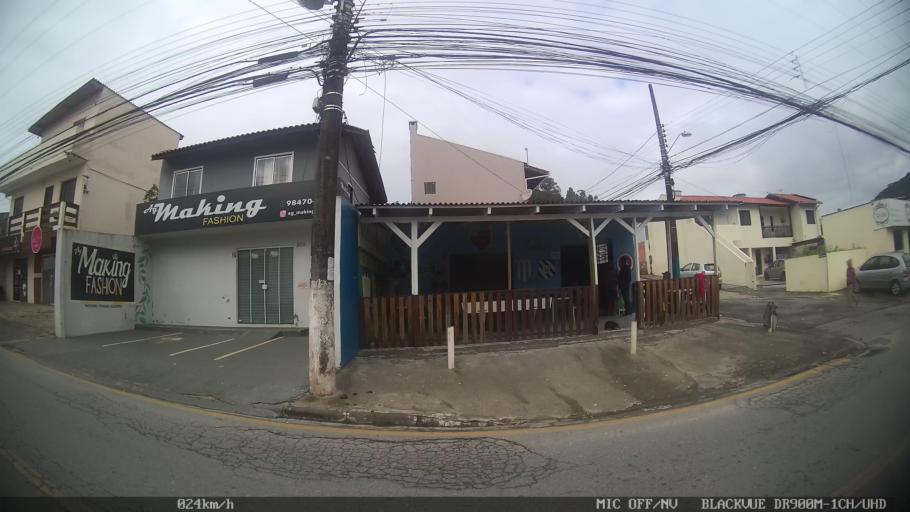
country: BR
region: Santa Catarina
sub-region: Biguacu
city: Biguacu
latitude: -27.5461
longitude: -48.6426
